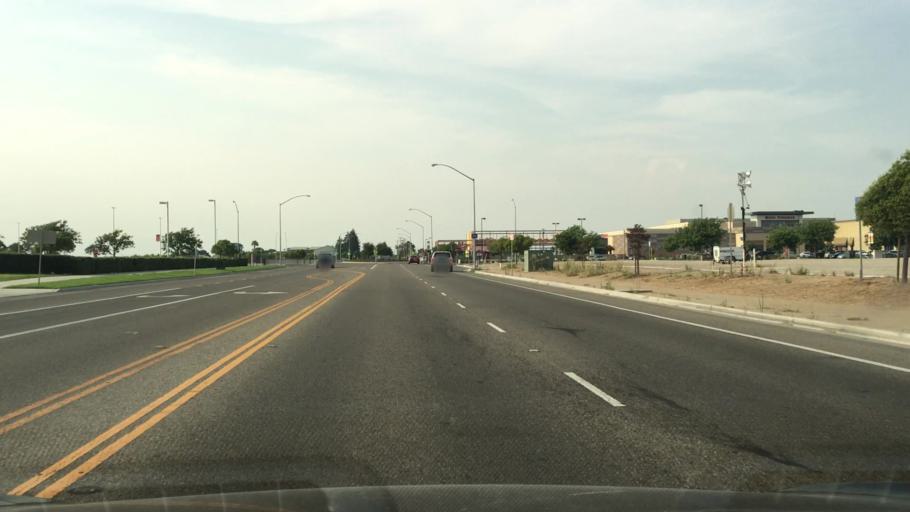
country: US
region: California
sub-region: Fresno County
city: Clovis
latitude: 36.8095
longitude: -119.7363
